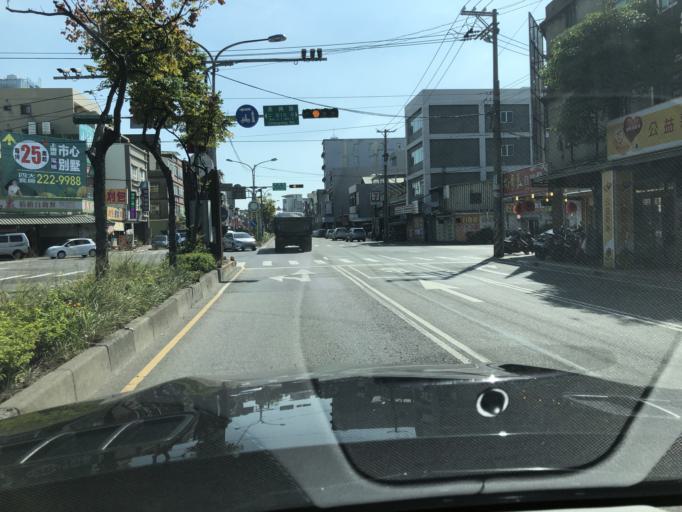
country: TW
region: Taiwan
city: Taoyuan City
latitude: 25.0739
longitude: 121.2854
